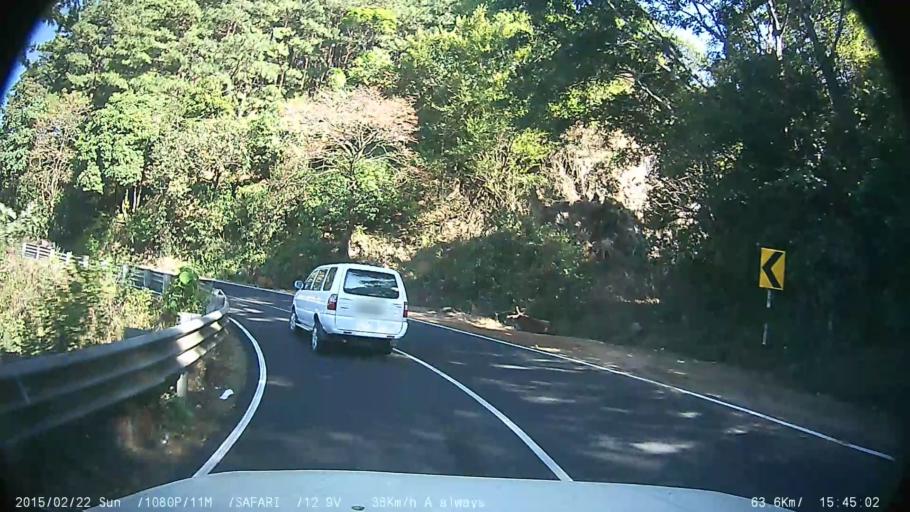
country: IN
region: Kerala
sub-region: Kottayam
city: Erattupetta
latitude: 9.5807
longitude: 76.9762
